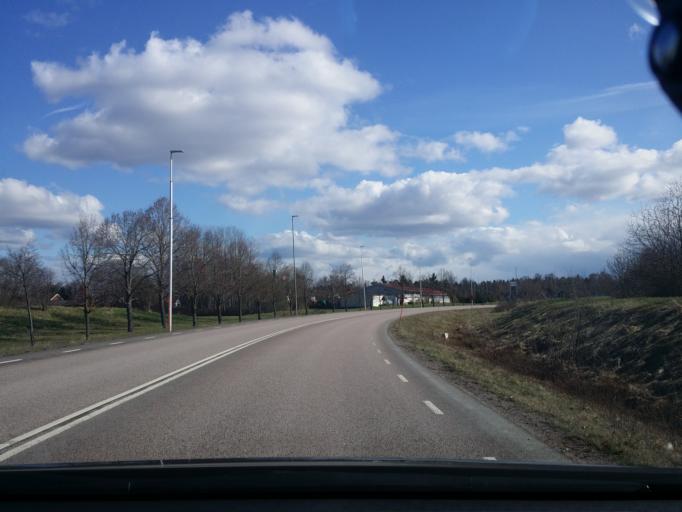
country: SE
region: Vaestmanland
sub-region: Sala Kommun
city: Sala
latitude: 59.9348
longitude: 16.5733
